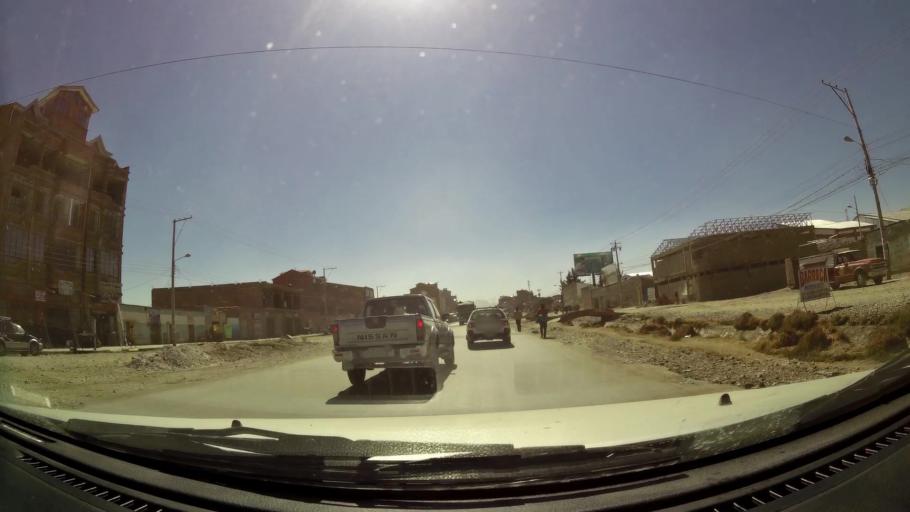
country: BO
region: La Paz
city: La Paz
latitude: -16.5386
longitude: -68.1939
